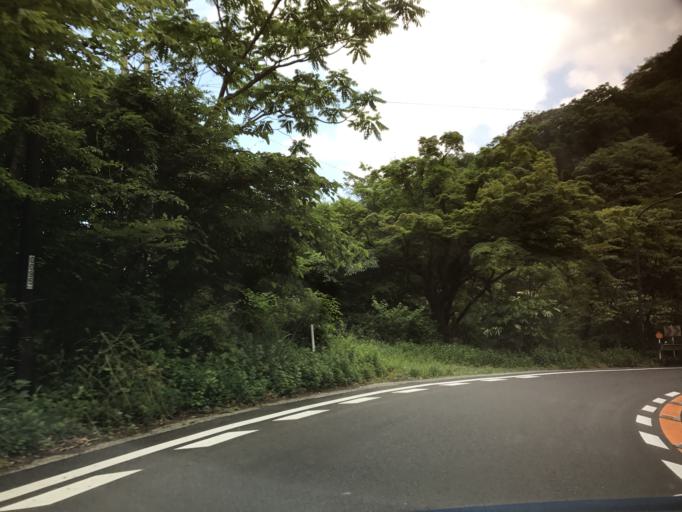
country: JP
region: Kanagawa
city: Hakone
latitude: 35.2331
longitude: 139.0824
